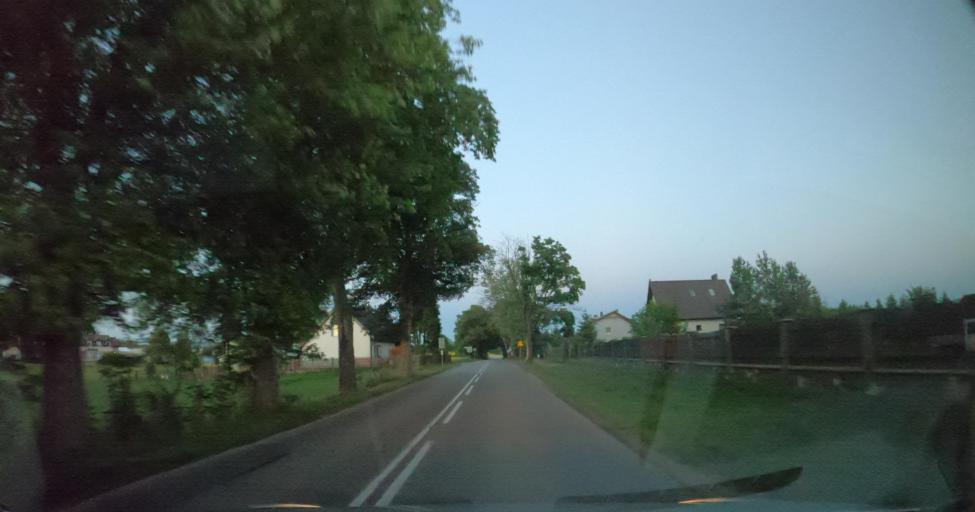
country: PL
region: Pomeranian Voivodeship
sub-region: Powiat wejherowski
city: Szemud
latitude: 54.4715
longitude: 18.2761
